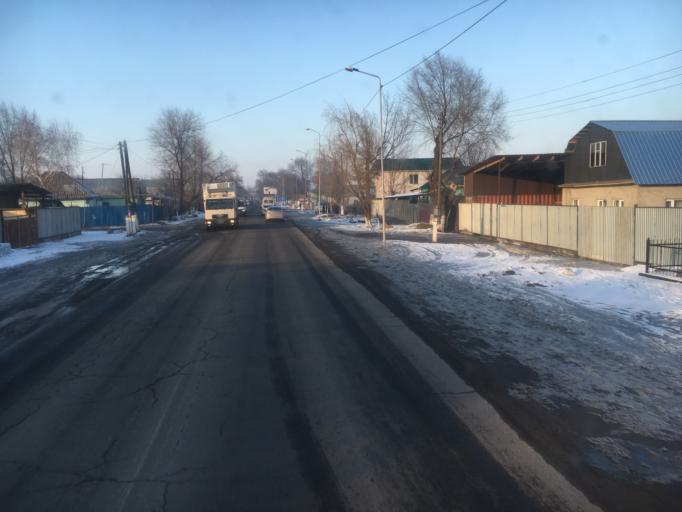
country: KZ
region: Almaty Oblysy
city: Burunday
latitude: 43.3726
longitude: 76.6417
